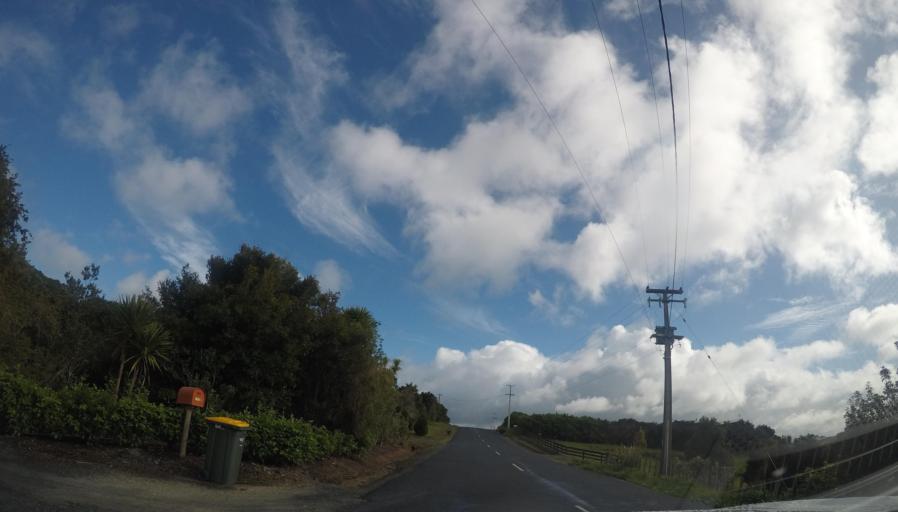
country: NZ
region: Auckland
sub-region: Auckland
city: Warkworth
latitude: -36.4664
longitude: 174.7358
